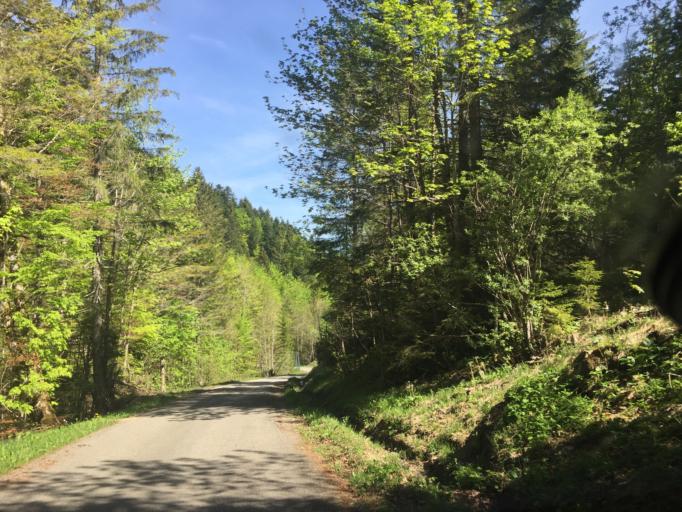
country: FR
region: Rhone-Alpes
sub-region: Departement de l'Isere
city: Le Sappey-en-Chartreuse
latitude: 45.2932
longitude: 5.8098
